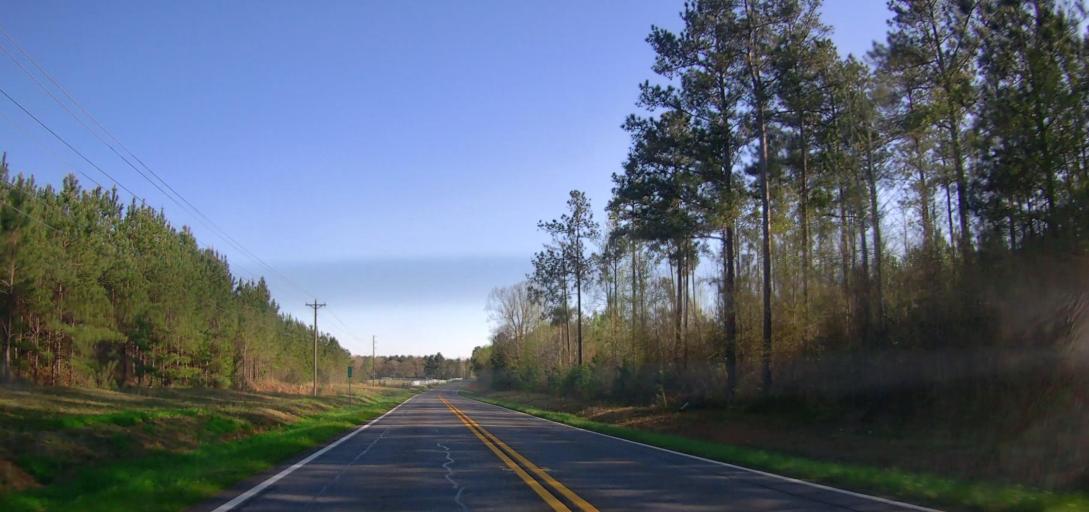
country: US
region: Georgia
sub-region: Butts County
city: Indian Springs
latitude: 33.1664
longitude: -83.9575
